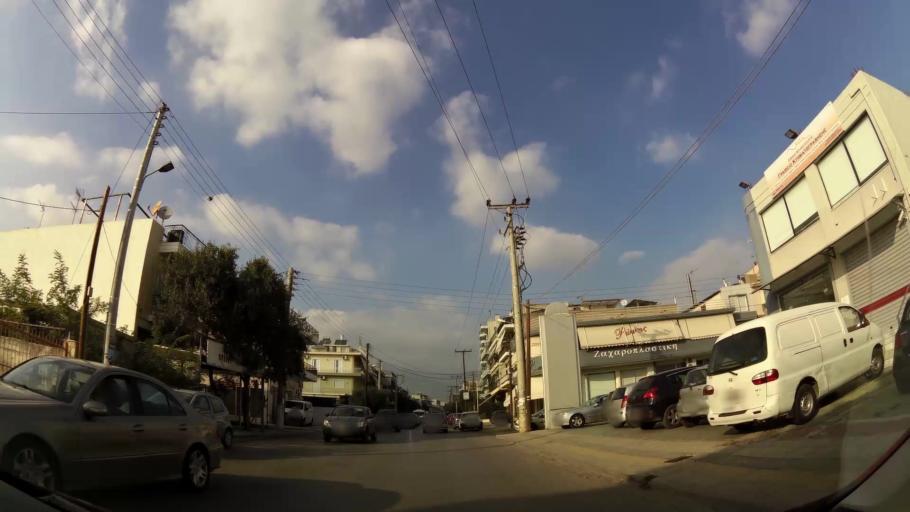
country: GR
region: Attica
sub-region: Nomarchia Anatolikis Attikis
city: Acharnes
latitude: 38.0836
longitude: 23.7303
